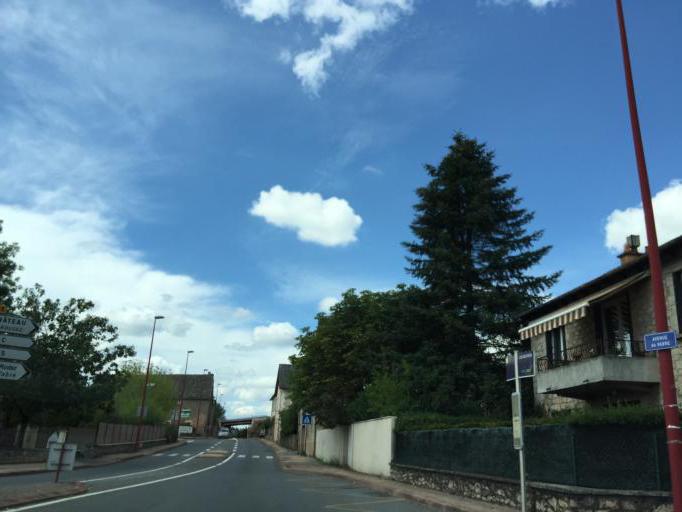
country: FR
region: Midi-Pyrenees
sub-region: Departement de l'Aveyron
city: Rodez
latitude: 44.3652
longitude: 2.5743
